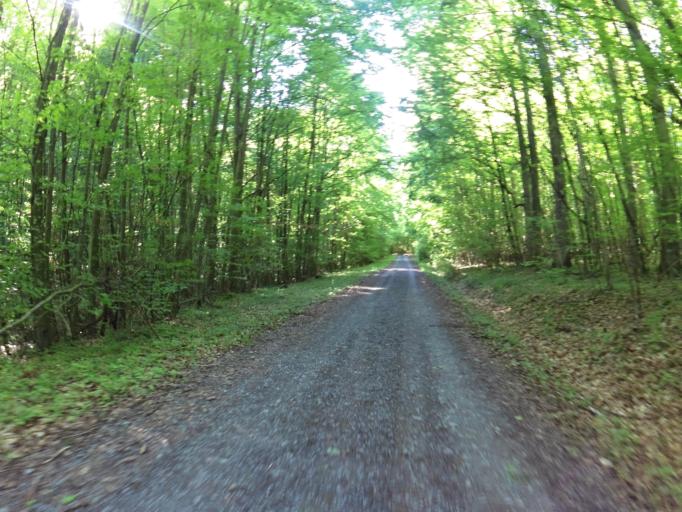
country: DE
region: Bavaria
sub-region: Regierungsbezirk Unterfranken
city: Reichenberg
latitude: 49.7424
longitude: 9.9196
